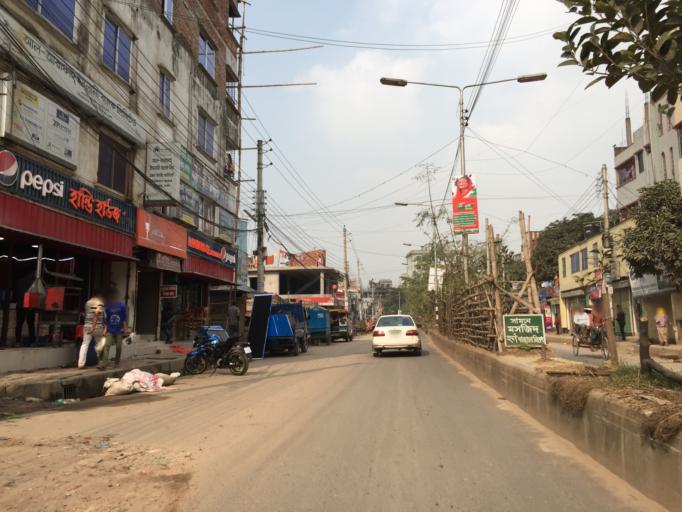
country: BD
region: Dhaka
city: Azimpur
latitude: 23.7891
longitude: 90.3664
